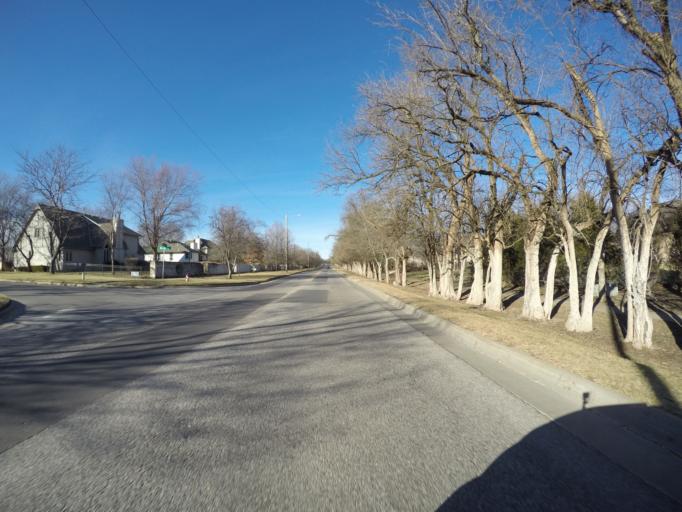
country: US
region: Kansas
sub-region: Sedgwick County
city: Maize
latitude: 37.7039
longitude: -97.4809
